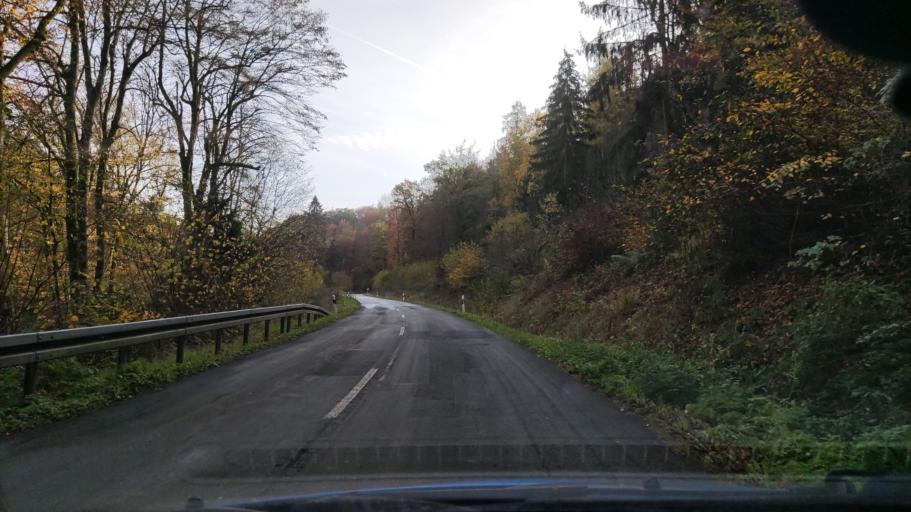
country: DE
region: Lower Saxony
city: Deensen
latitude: 51.8915
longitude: 9.5957
